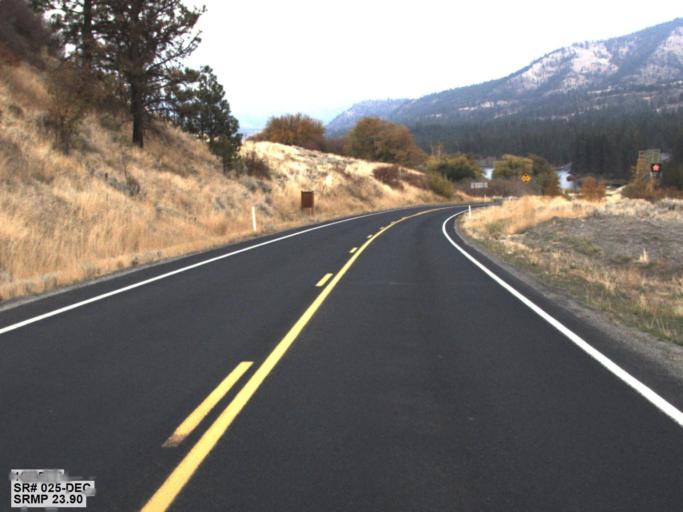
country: US
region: Washington
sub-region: Lincoln County
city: Davenport
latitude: 47.9071
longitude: -118.3272
